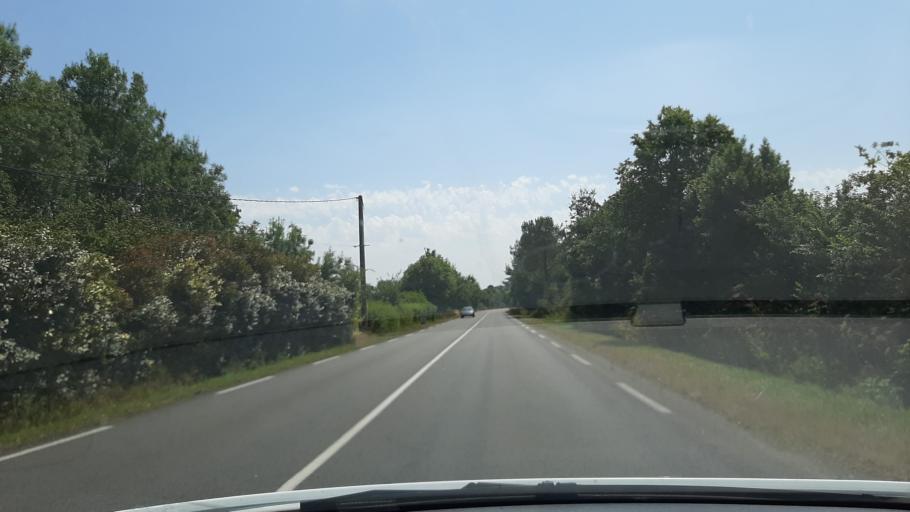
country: FR
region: Pays de la Loire
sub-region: Departement de la Vendee
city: Mouilleron-le-Captif
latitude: 46.7498
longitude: -1.4579
